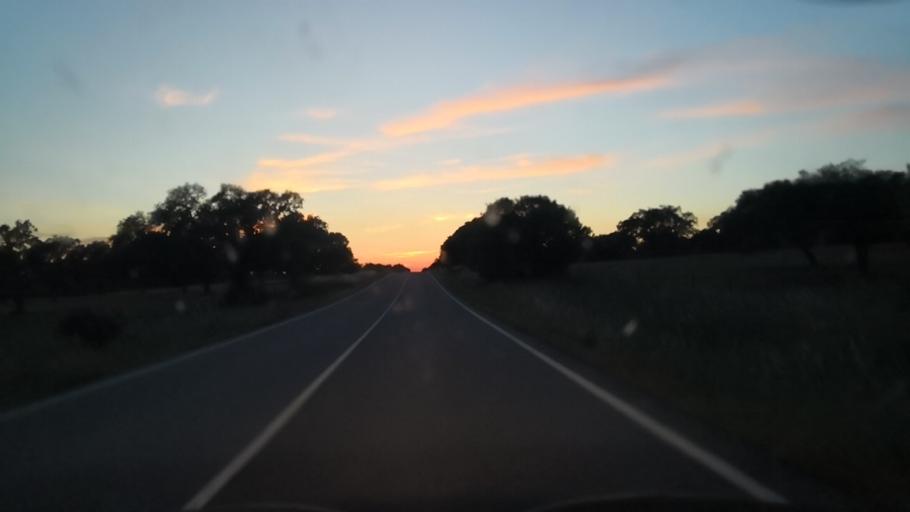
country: ES
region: Extremadura
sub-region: Provincia de Caceres
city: Piedras Albas
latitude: 39.7835
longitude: -6.9374
